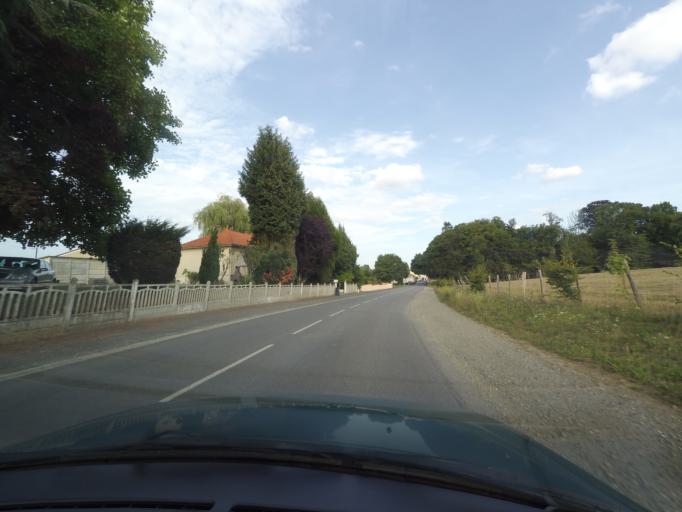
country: FR
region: Limousin
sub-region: Departement de la Haute-Vienne
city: Sereilhac
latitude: 45.7659
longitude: 1.0749
